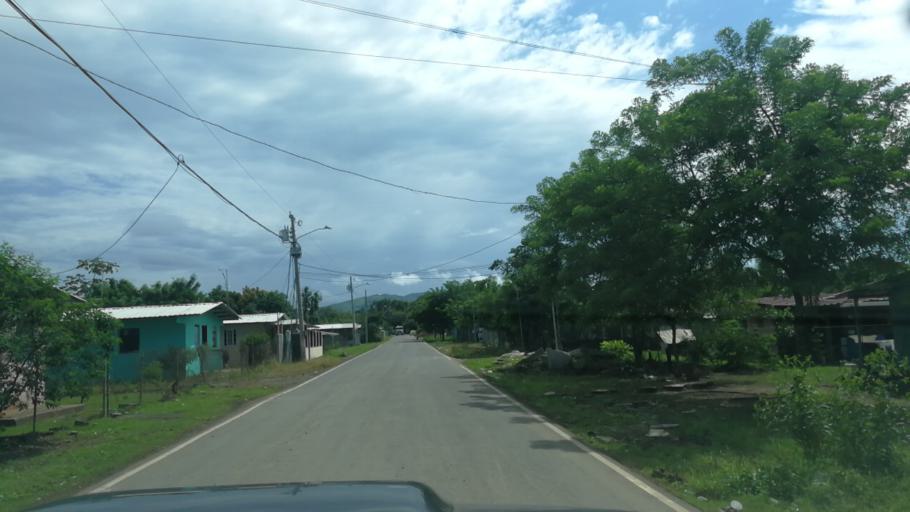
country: PA
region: Panama
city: Paso Blanco
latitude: 9.1348
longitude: -79.2535
